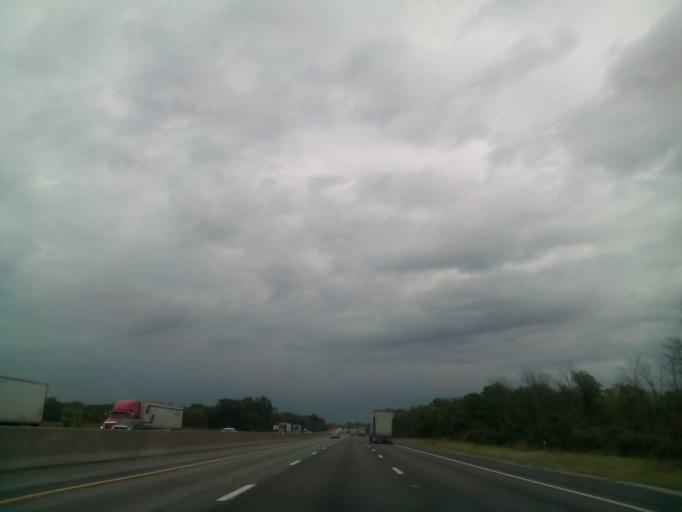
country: US
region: Ohio
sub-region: Ottawa County
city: Elmore
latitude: 41.4695
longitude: -83.3168
